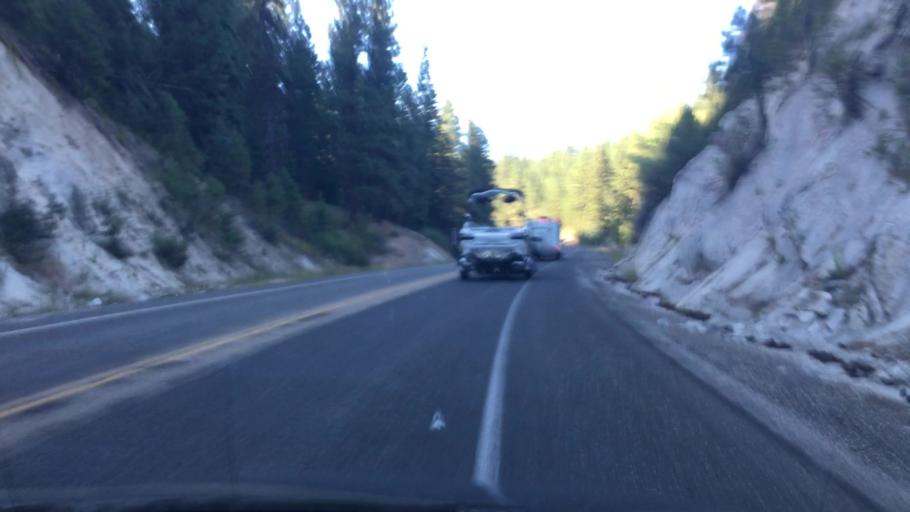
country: US
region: Idaho
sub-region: Valley County
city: Cascade
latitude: 44.5662
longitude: -116.0302
